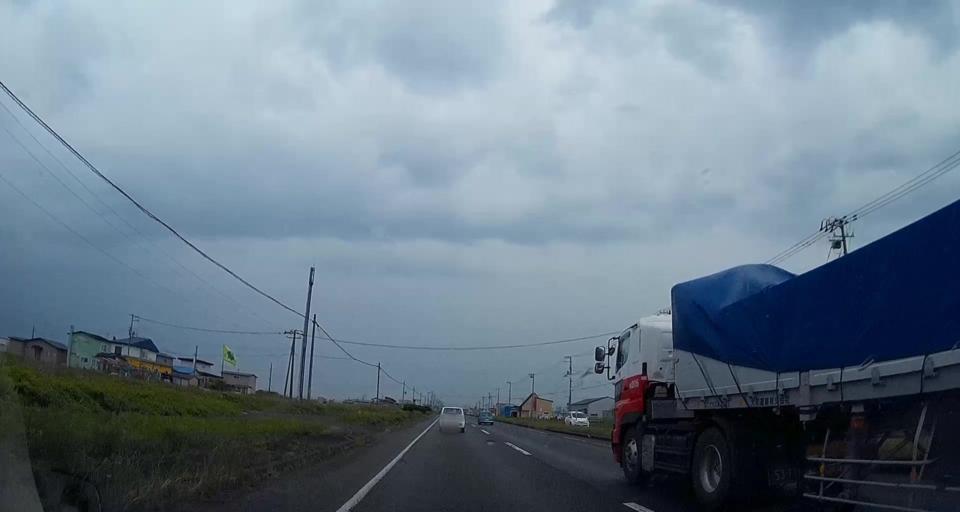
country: JP
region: Hokkaido
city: Tomakomai
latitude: 42.6016
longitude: 141.4873
